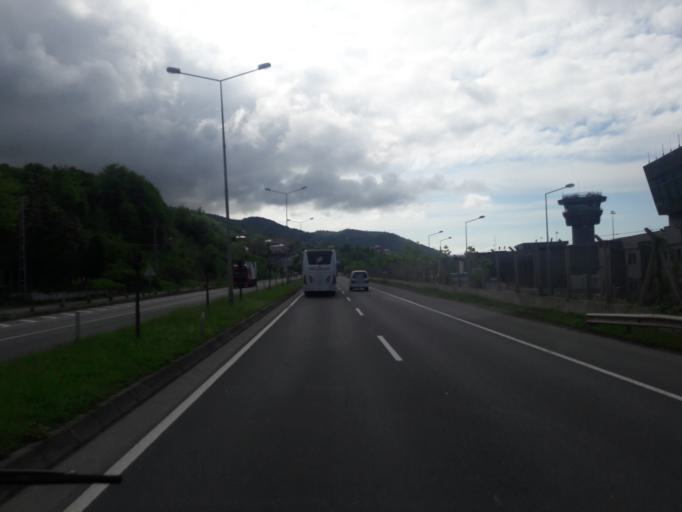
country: TR
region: Ordu
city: Gulyali
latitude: 40.9629
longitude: 38.0851
